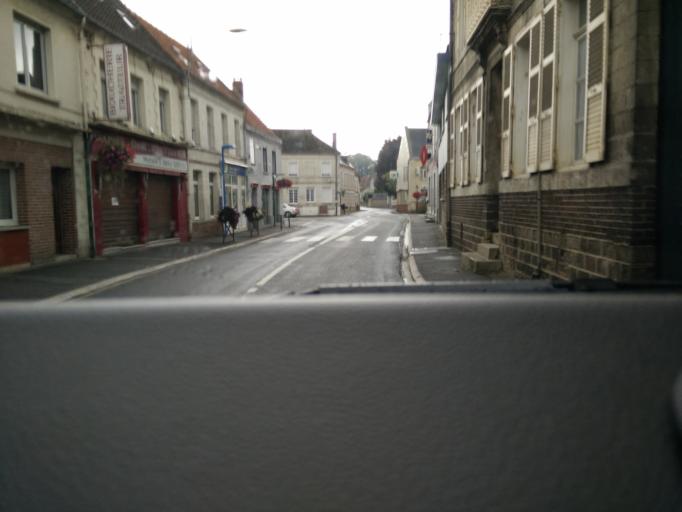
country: FR
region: Nord-Pas-de-Calais
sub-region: Departement du Pas-de-Calais
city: Aubigny-en-Artois
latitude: 50.3513
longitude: 2.5910
